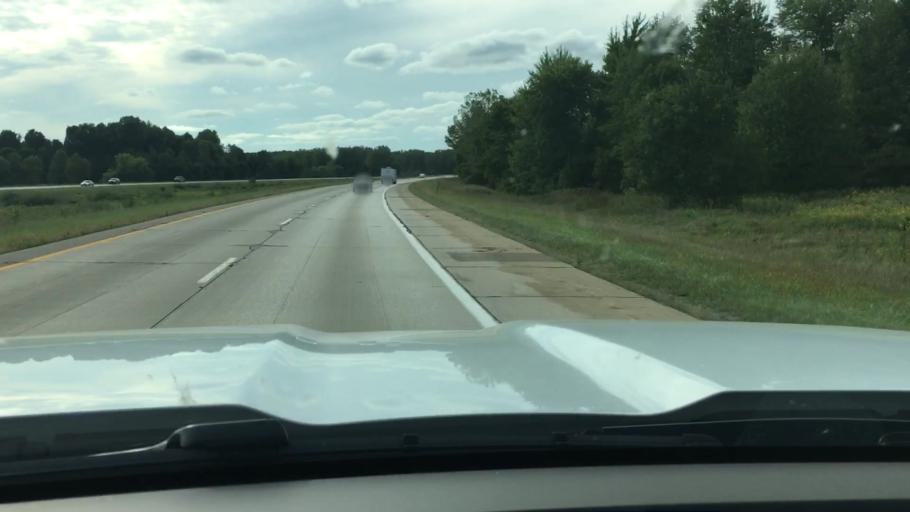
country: US
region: Michigan
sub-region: Lapeer County
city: Imlay City
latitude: 42.9966
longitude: -83.1321
